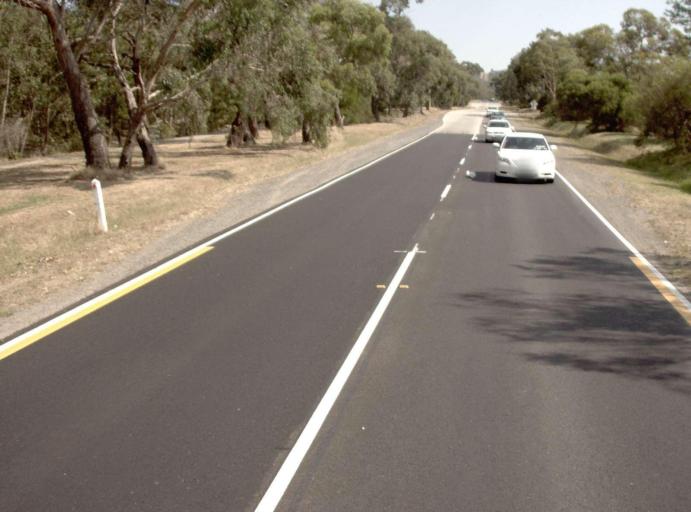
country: AU
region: Victoria
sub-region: Yarra Ranges
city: Lysterfield
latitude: -37.9159
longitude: 145.2714
